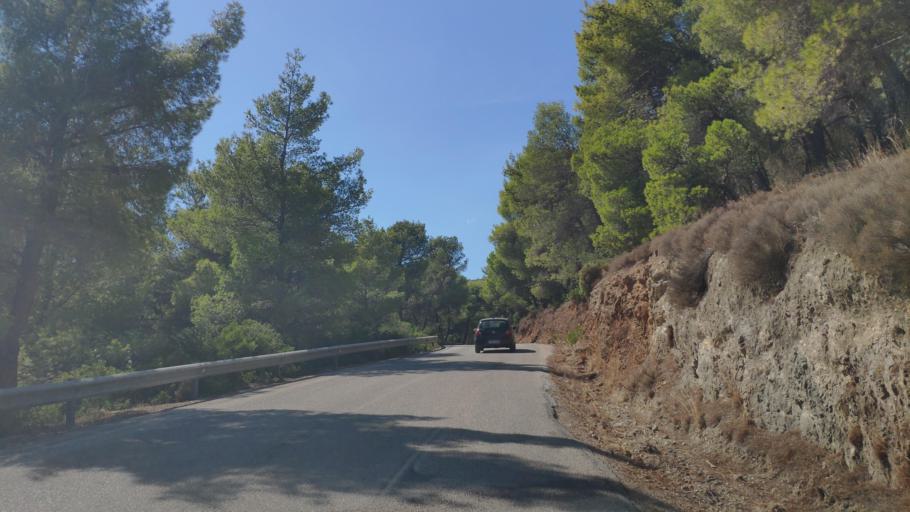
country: GR
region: Attica
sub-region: Nomarchia Anatolikis Attikis
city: Kouvaras
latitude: 37.8401
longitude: 24.0108
